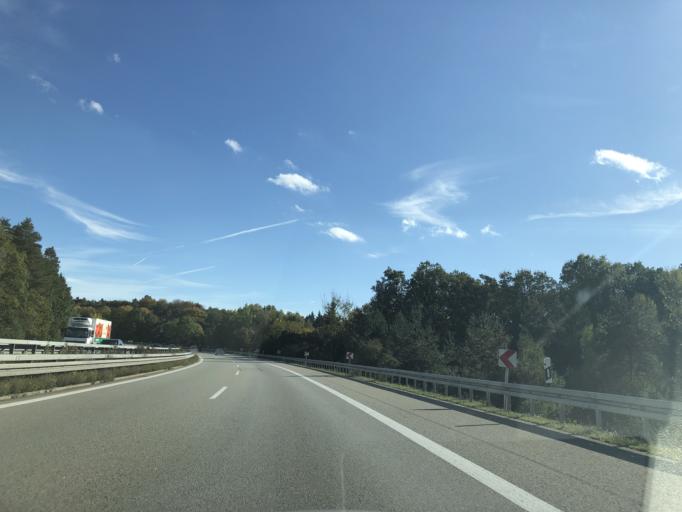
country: DE
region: Bavaria
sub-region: Upper Palatinate
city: Sinzing
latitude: 48.9960
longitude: 12.0051
